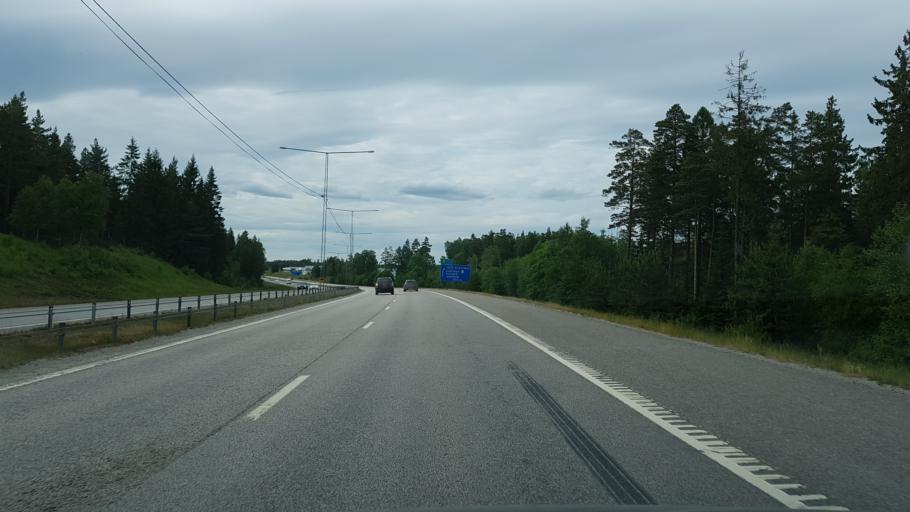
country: SE
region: Stockholm
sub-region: Haninge Kommun
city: Haninge
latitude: 59.1423
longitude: 18.1613
